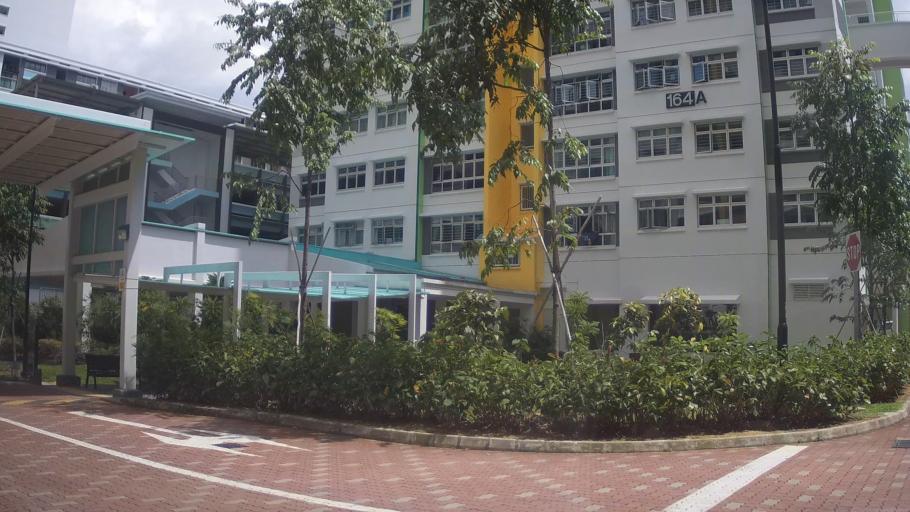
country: SG
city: Singapore
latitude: 1.3308
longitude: 103.7217
